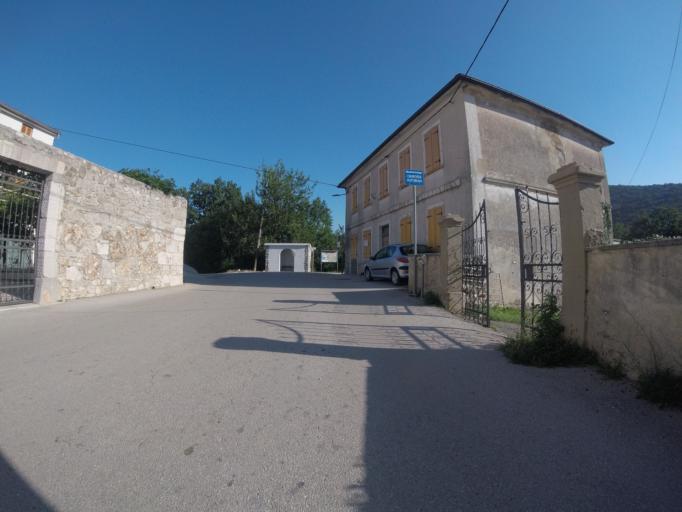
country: HR
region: Primorsko-Goranska
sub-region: Grad Crikvenica
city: Jadranovo
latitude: 45.2490
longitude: 14.6278
